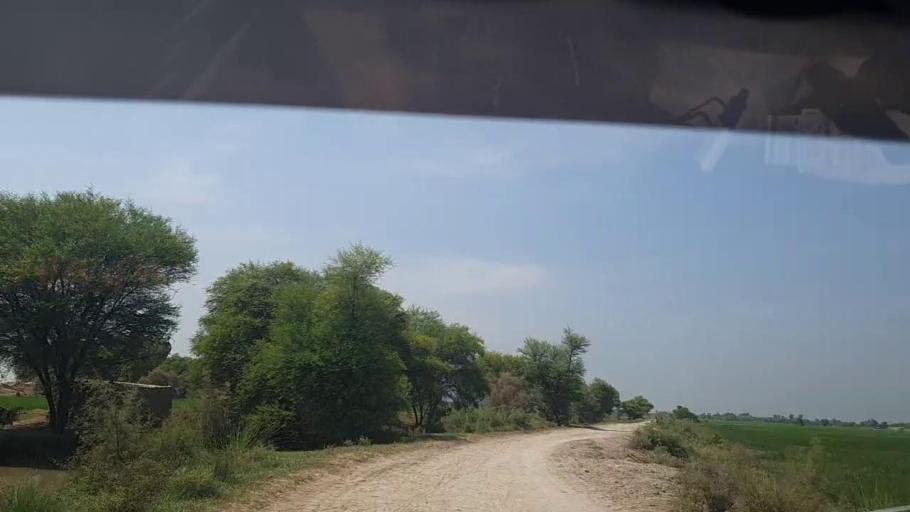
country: PK
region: Sindh
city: Thul
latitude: 28.1921
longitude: 68.7116
